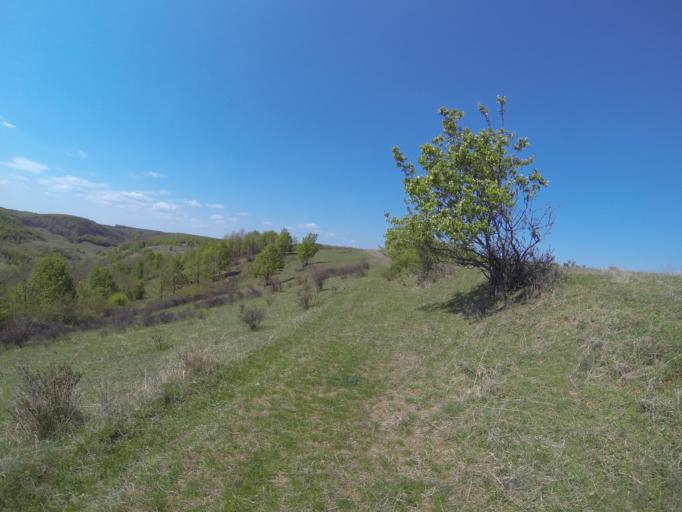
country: RO
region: Gorj
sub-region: Comuna Crusetu
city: Crusetu
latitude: 44.6085
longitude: 23.6496
